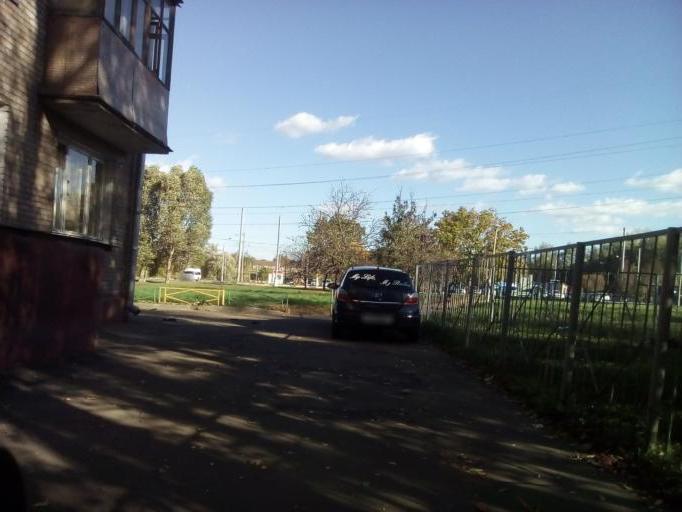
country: RU
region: Moscow
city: Novovladykino
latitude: 55.8465
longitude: 37.5885
